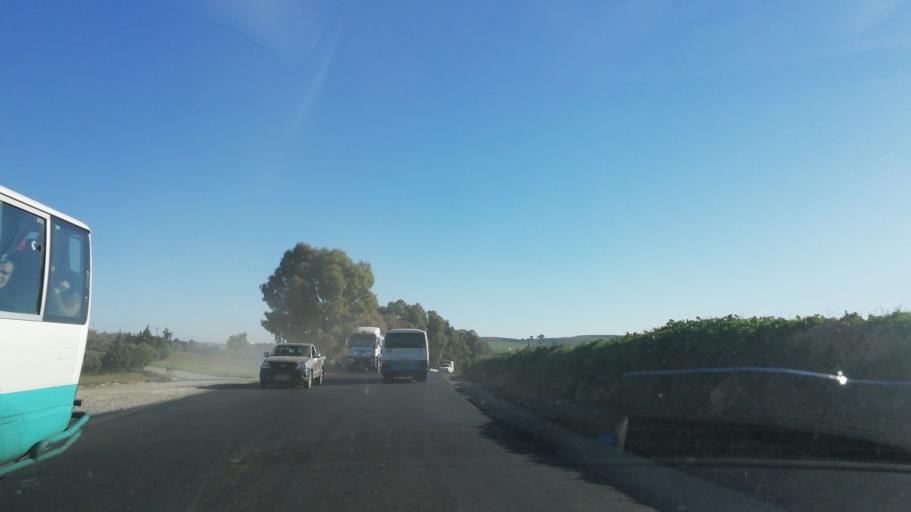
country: DZ
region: Relizane
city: Smala
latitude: 35.6736
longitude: 0.8034
